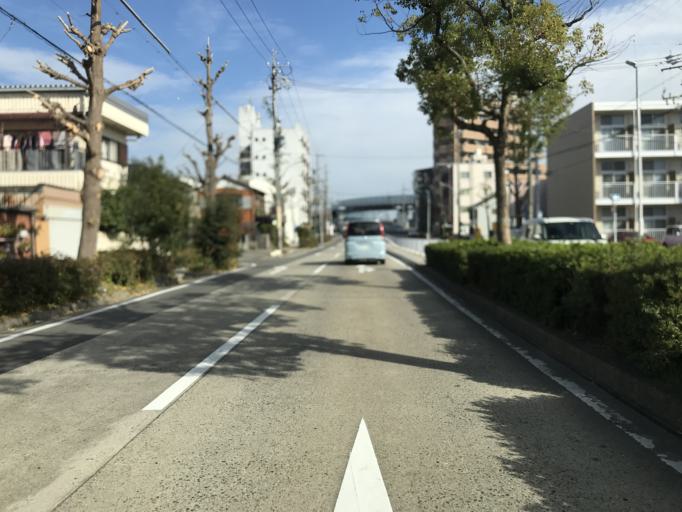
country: JP
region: Aichi
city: Nagoya-shi
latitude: 35.2066
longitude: 136.9276
